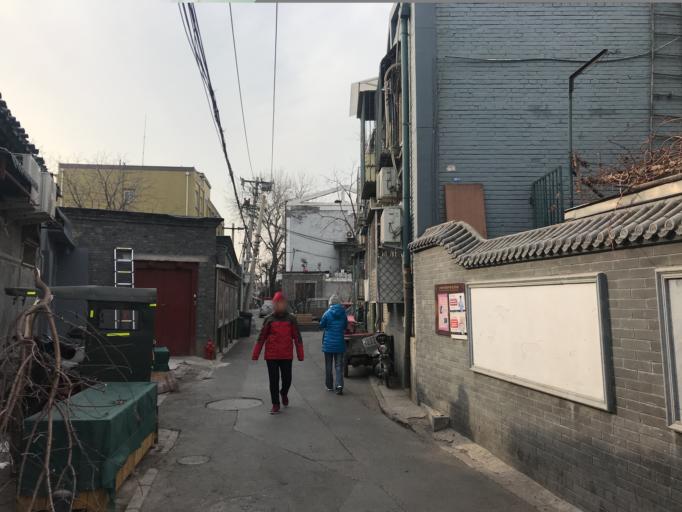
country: CN
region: Beijing
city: Beijing
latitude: 39.8925
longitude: 116.3822
